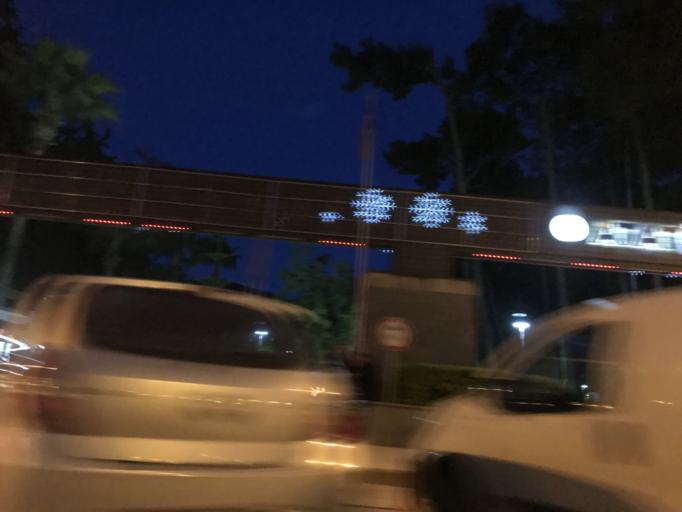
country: TR
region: Hatay
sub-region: Antakya Ilcesi
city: Antakya
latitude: 36.2012
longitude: 36.1583
